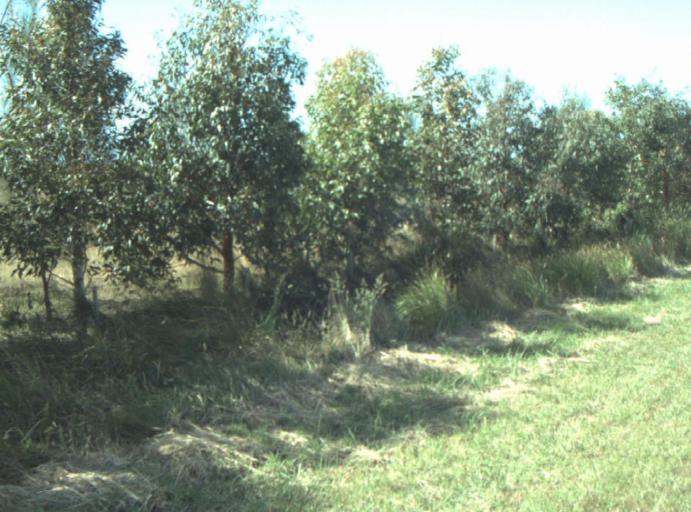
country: AU
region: Victoria
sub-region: Greater Geelong
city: Clifton Springs
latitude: -38.2391
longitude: 144.5752
